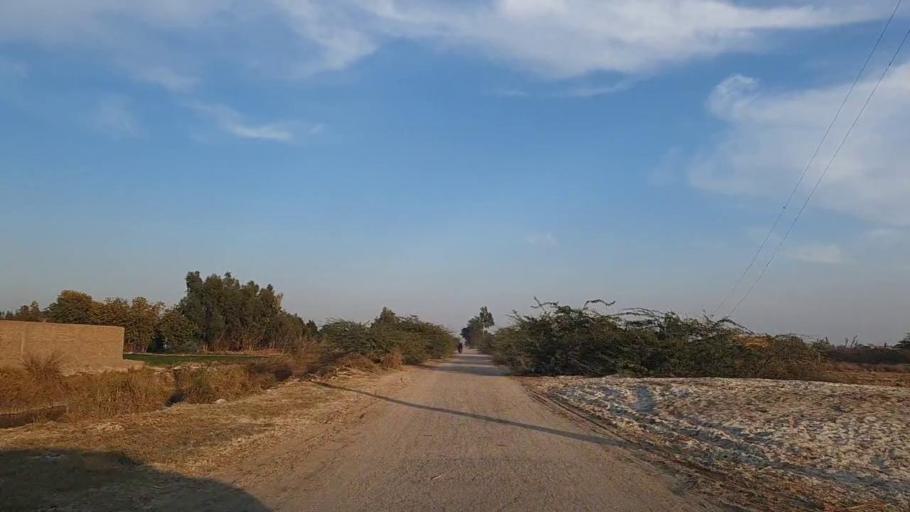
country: PK
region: Sindh
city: Bandhi
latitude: 26.5981
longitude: 68.3503
